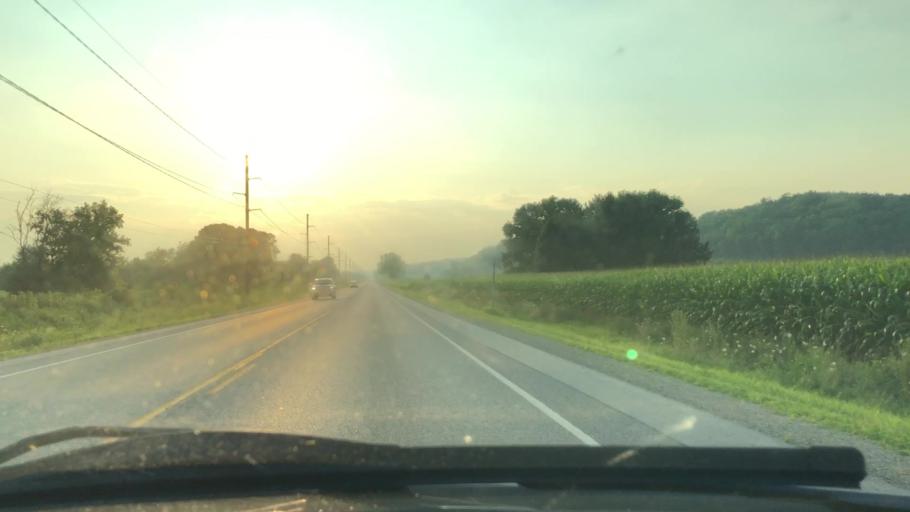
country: US
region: Wisconsin
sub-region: Dane County
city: Cross Plains
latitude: 43.1207
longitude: -89.6928
